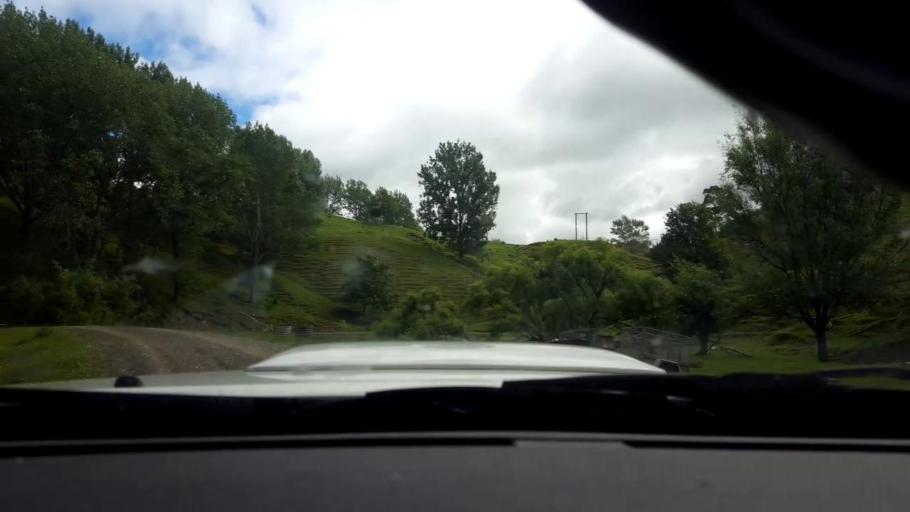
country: NZ
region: Gisborne
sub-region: Gisborne District
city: Gisborne
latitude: -38.4897
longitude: 177.6845
